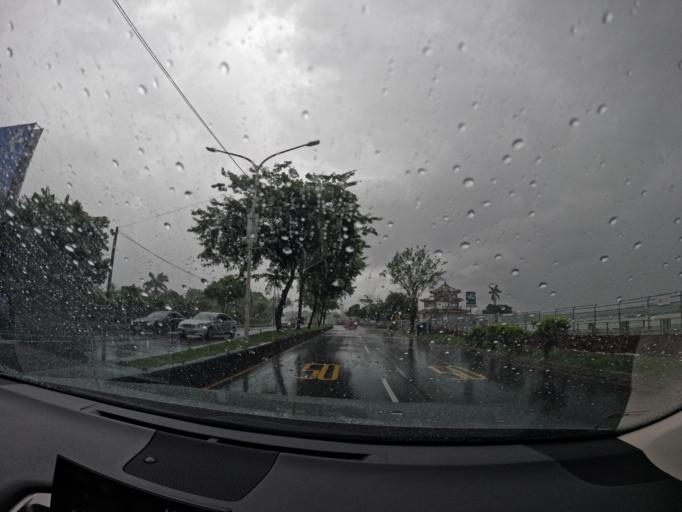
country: TW
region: Taiwan
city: Fengshan
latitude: 22.6576
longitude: 120.3587
